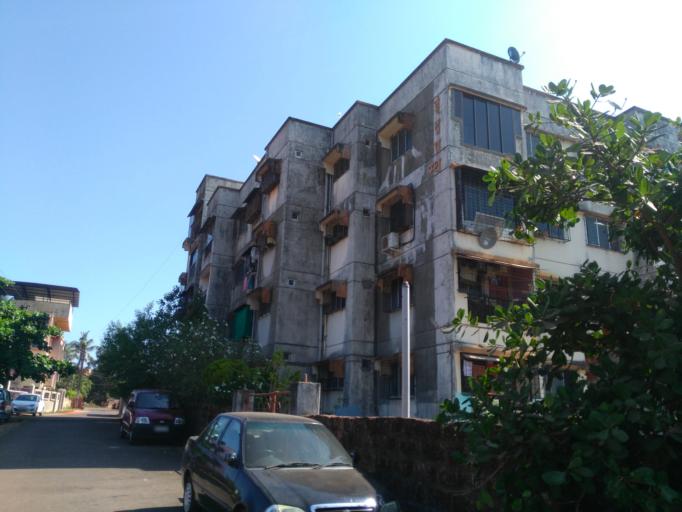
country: IN
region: Maharashtra
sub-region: Ratnagiri
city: Ratnagiri
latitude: 16.9824
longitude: 73.3141
